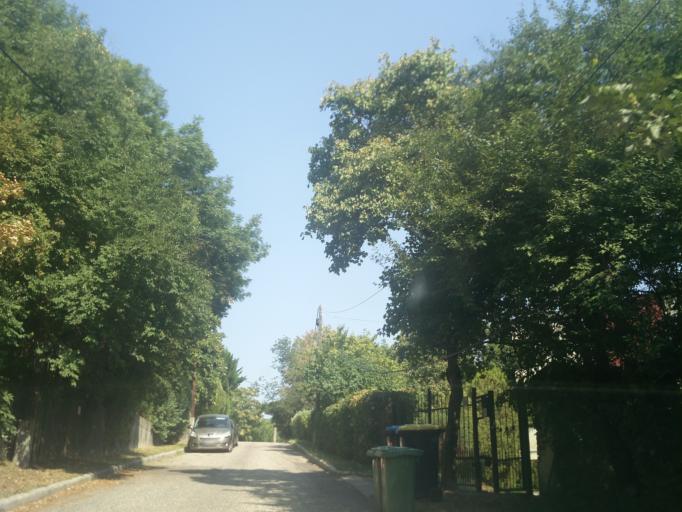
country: HU
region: Budapest
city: Budapest XII. keruelet
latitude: 47.4993
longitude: 19.0002
